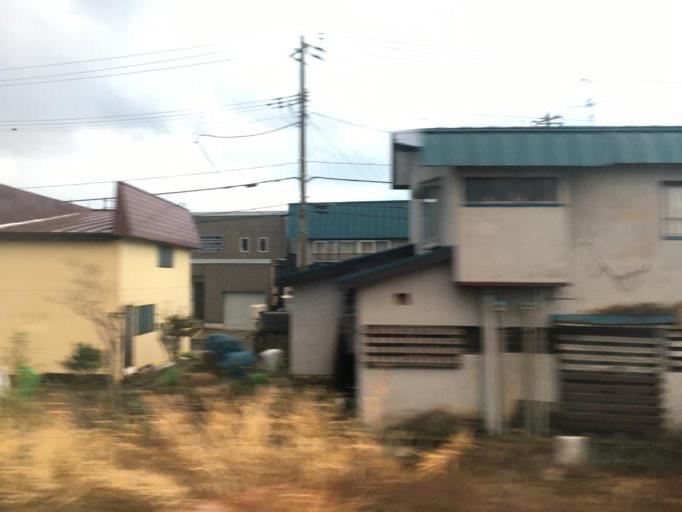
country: JP
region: Aomori
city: Aomori Shi
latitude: 40.8239
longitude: 140.7250
